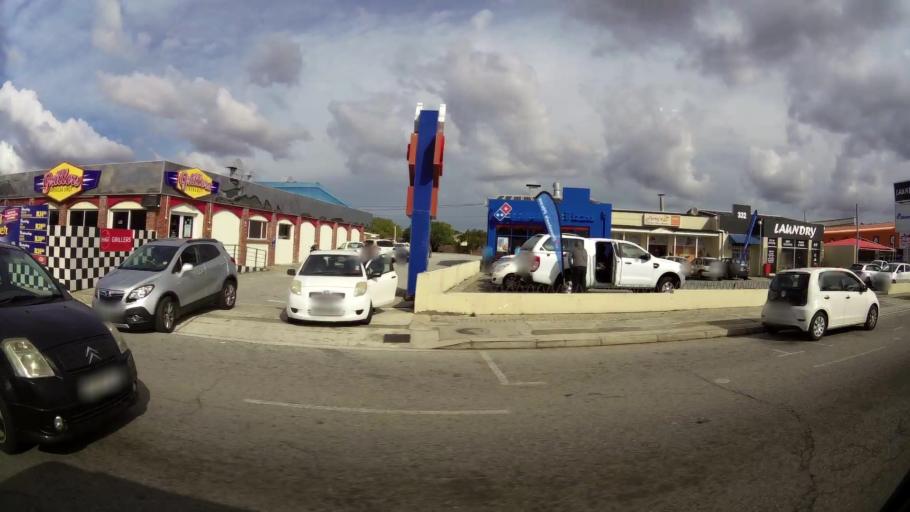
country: ZA
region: Eastern Cape
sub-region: Nelson Mandela Bay Metropolitan Municipality
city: Port Elizabeth
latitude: -33.9482
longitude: 25.5602
